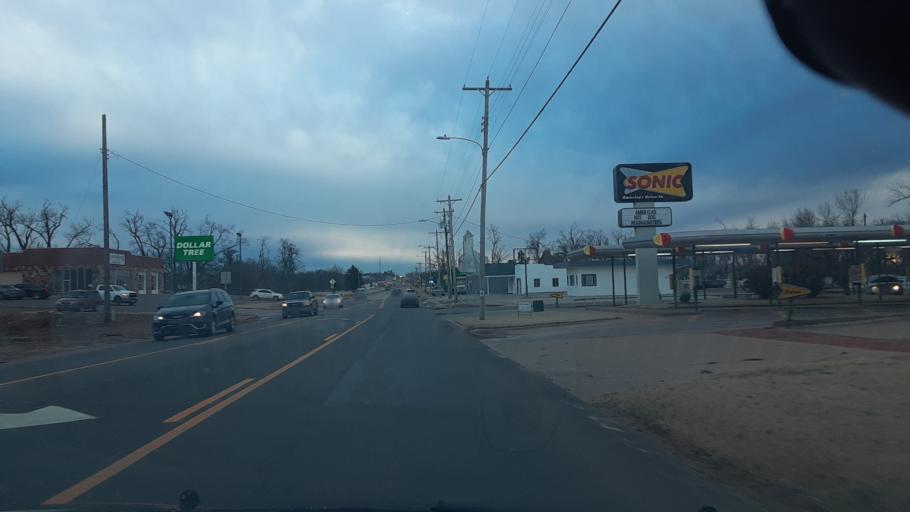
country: US
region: Oklahoma
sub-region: Logan County
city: Guthrie
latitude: 35.8713
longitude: -97.4254
